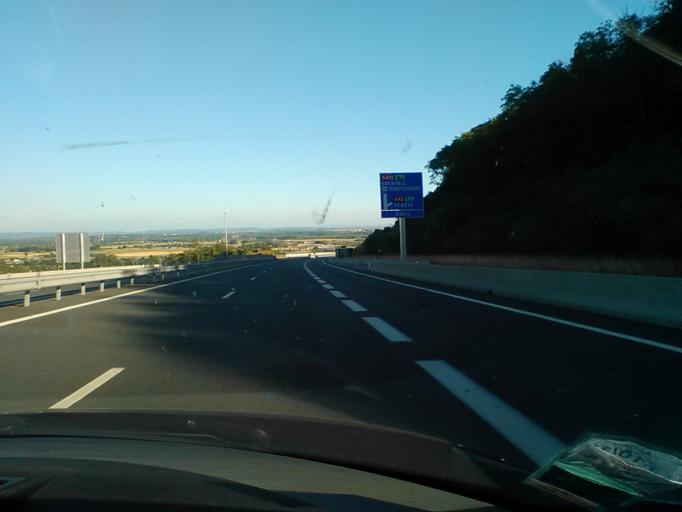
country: FR
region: Rhone-Alpes
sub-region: Departement de l'Ain
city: Beynost
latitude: 45.8464
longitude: 5.0133
